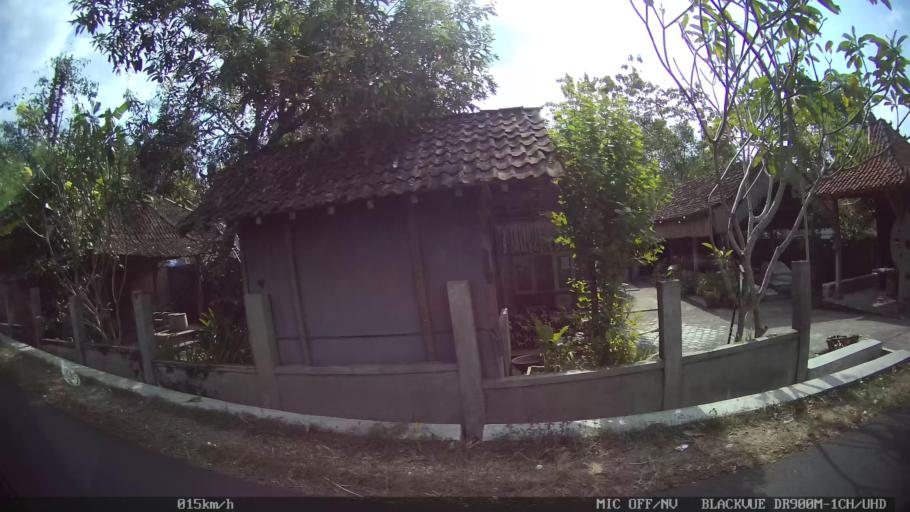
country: ID
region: Daerah Istimewa Yogyakarta
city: Kasihan
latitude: -7.8512
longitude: 110.3139
